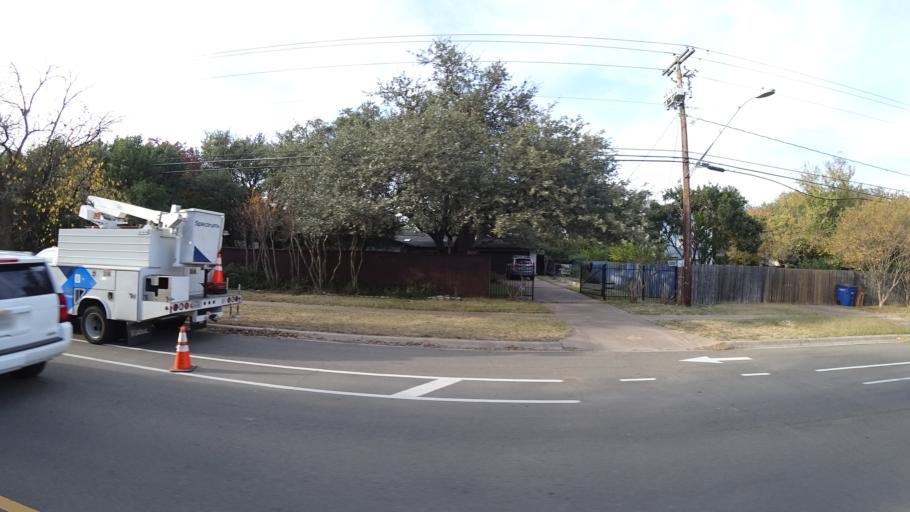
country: US
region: Texas
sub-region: Williamson County
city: Jollyville
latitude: 30.3811
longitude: -97.7491
